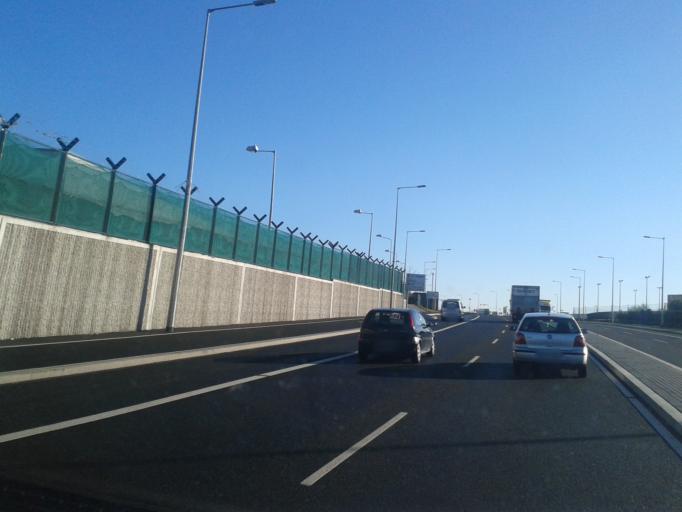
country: IE
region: Leinster
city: Beaumont
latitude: 53.4209
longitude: -6.2329
